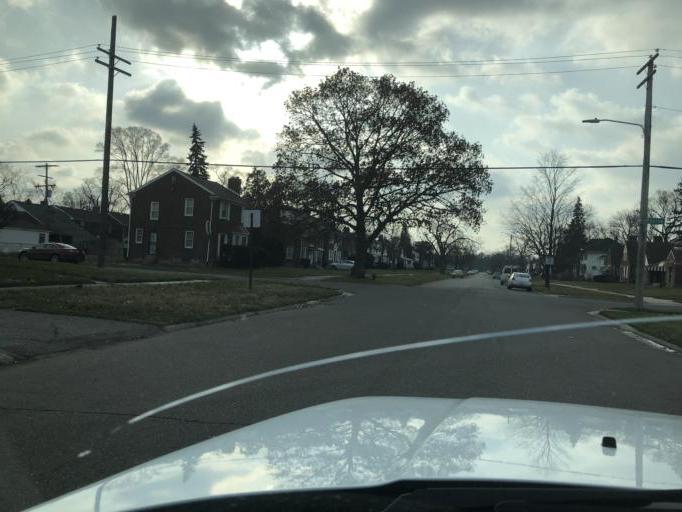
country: US
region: Michigan
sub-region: Oakland County
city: Oak Park
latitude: 42.4123
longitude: -83.2155
